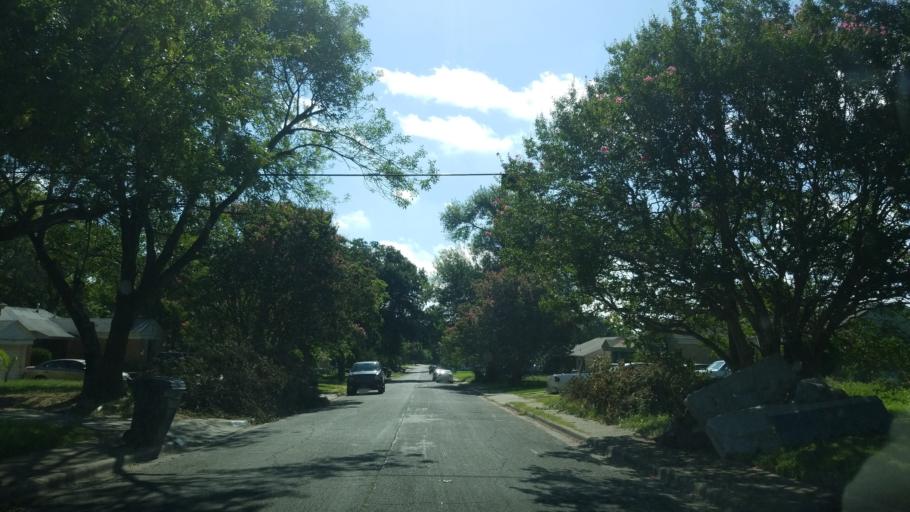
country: US
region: Texas
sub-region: Dallas County
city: Dallas
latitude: 32.7161
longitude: -96.8028
